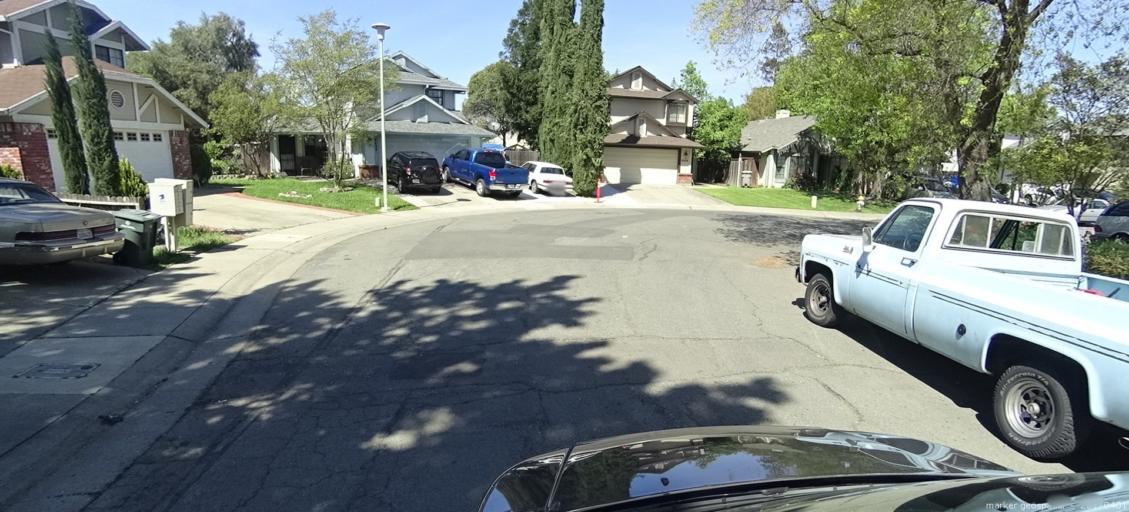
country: US
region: California
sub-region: Sacramento County
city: Laguna
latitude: 38.4503
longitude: -121.4332
